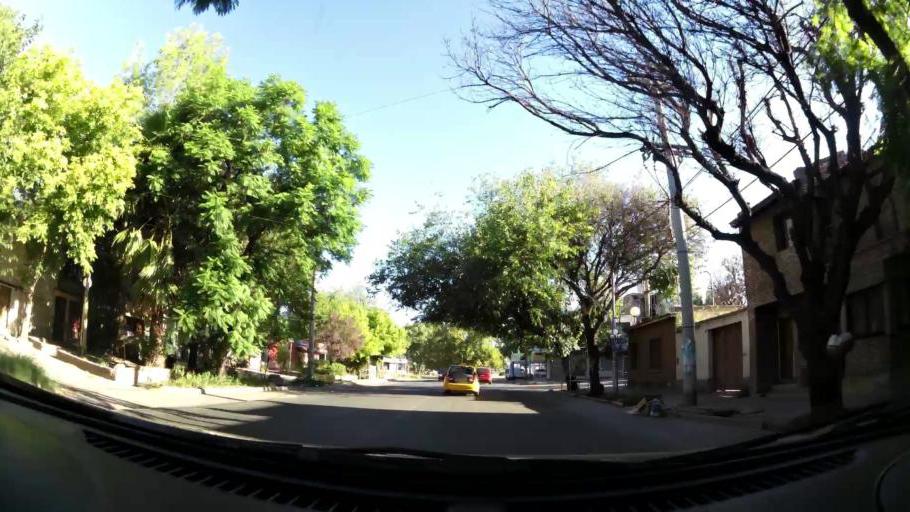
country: AR
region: Mendoza
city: Las Heras
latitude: -32.8658
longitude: -68.8289
